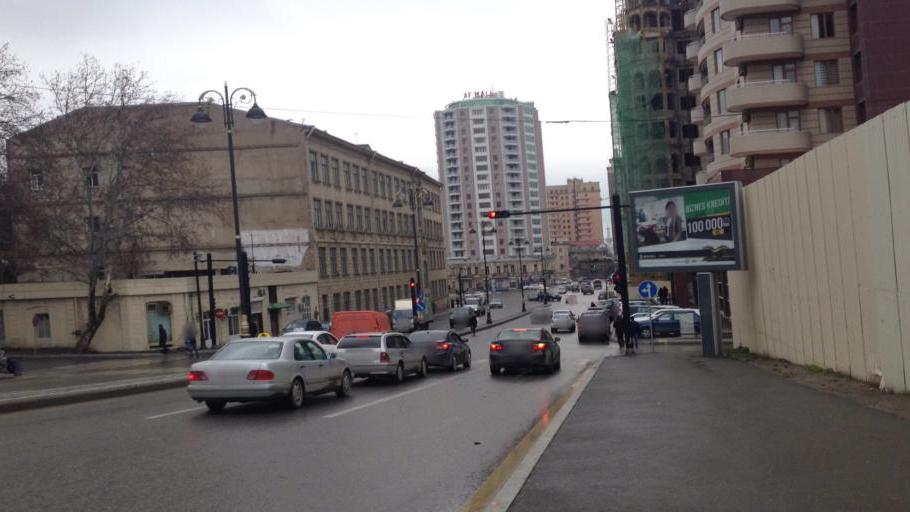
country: AZ
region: Baki
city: Baku
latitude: 40.3792
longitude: 49.8398
